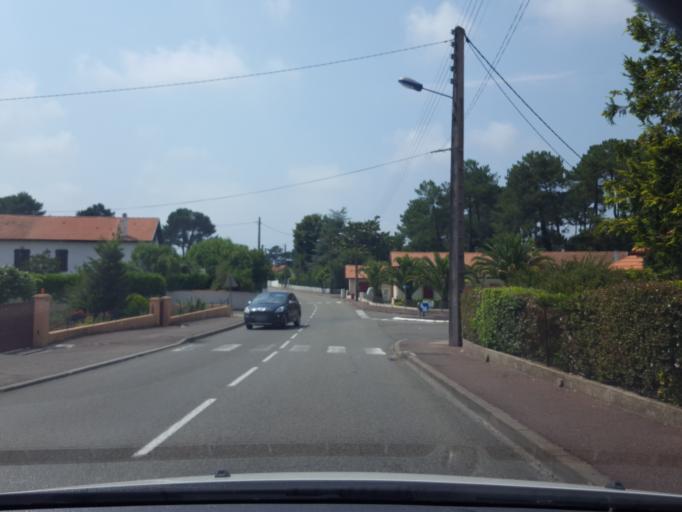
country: FR
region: Aquitaine
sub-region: Departement des Landes
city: Ondres
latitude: 43.5670
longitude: -1.4452
